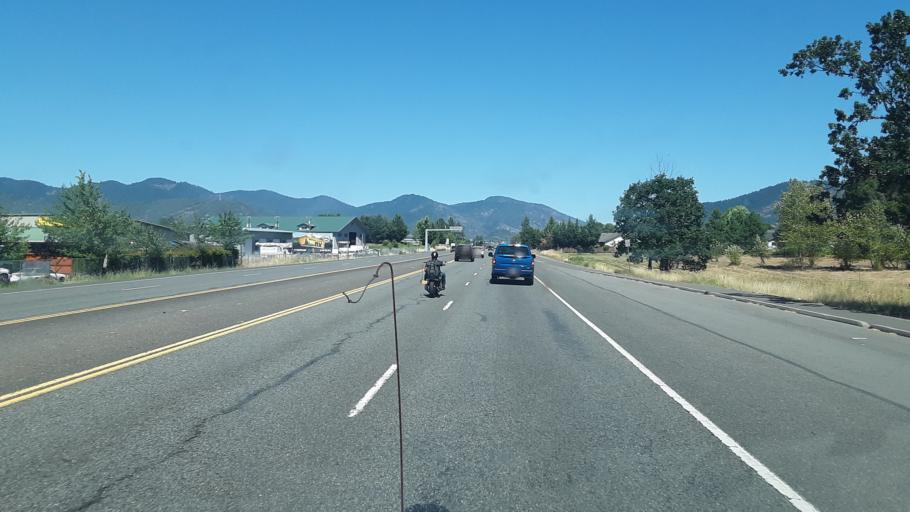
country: US
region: Oregon
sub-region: Josephine County
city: Redwood
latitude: 42.4198
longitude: -123.3598
